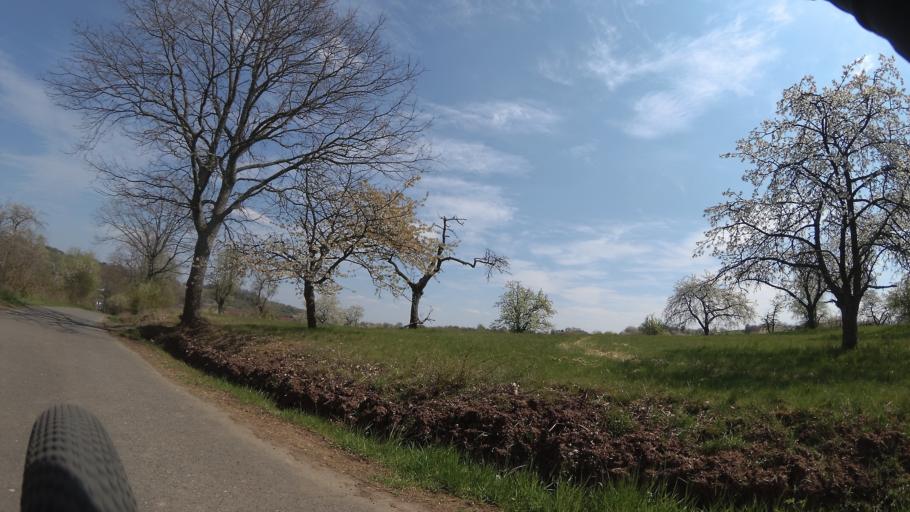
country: DE
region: Rheinland-Pfalz
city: Altenkirchen
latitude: 49.4396
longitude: 7.3144
